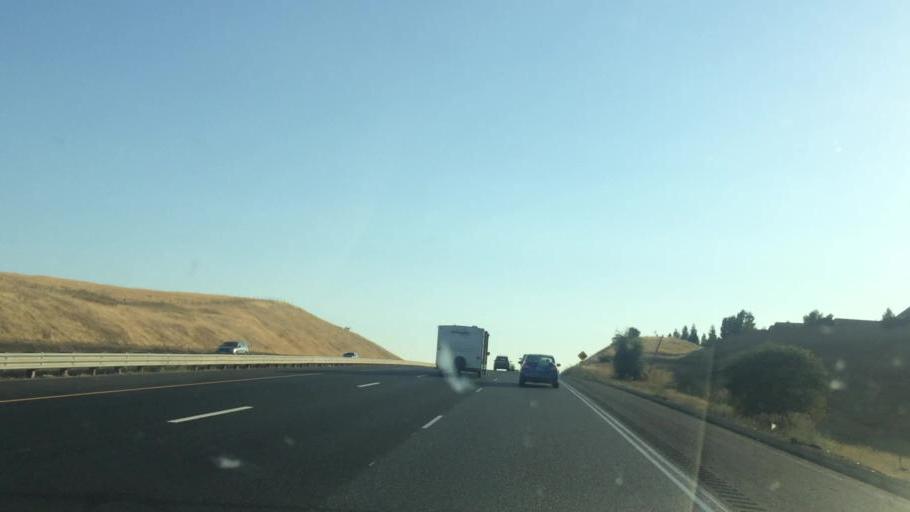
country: US
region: California
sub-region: El Dorado County
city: El Dorado Hills
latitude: 38.6460
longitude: -121.0918
